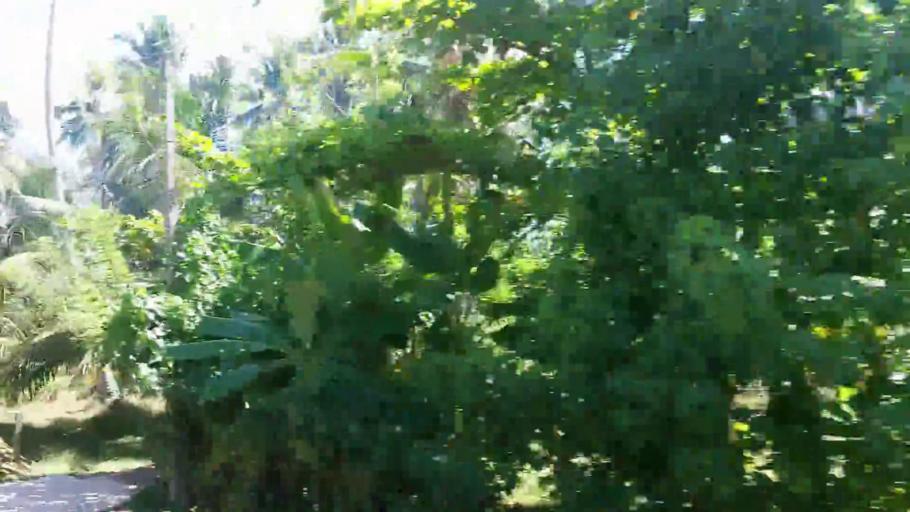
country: LK
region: Southern
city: Hikkaduwa
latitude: 6.1733
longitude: 80.0846
